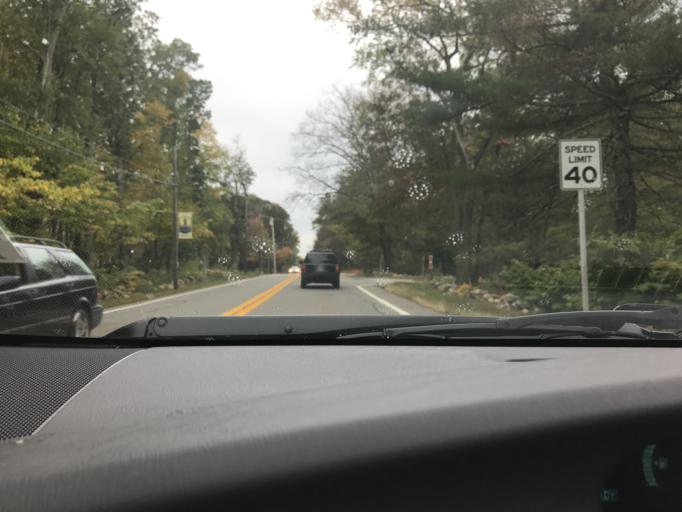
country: US
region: Massachusetts
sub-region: Middlesex County
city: Lincoln
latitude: 42.4511
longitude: -71.2923
